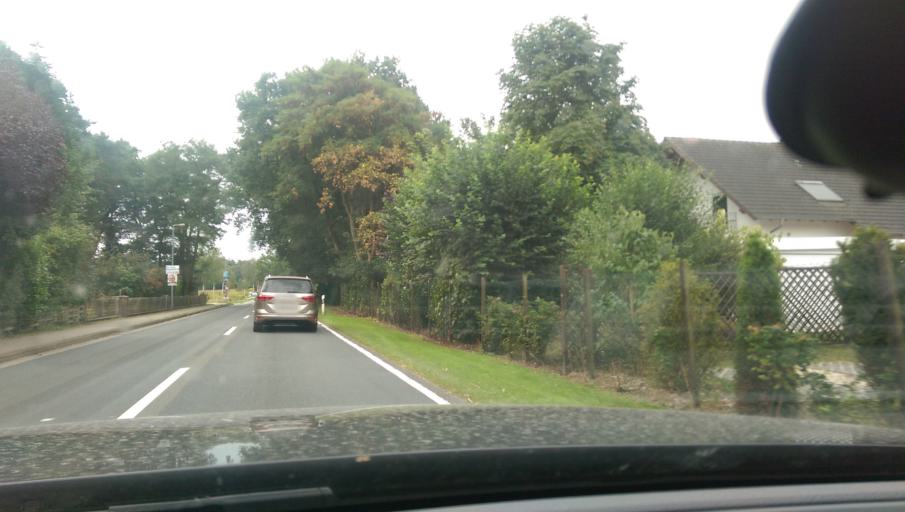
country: DE
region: Lower Saxony
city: Linsburg
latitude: 52.5239
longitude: 9.3299
